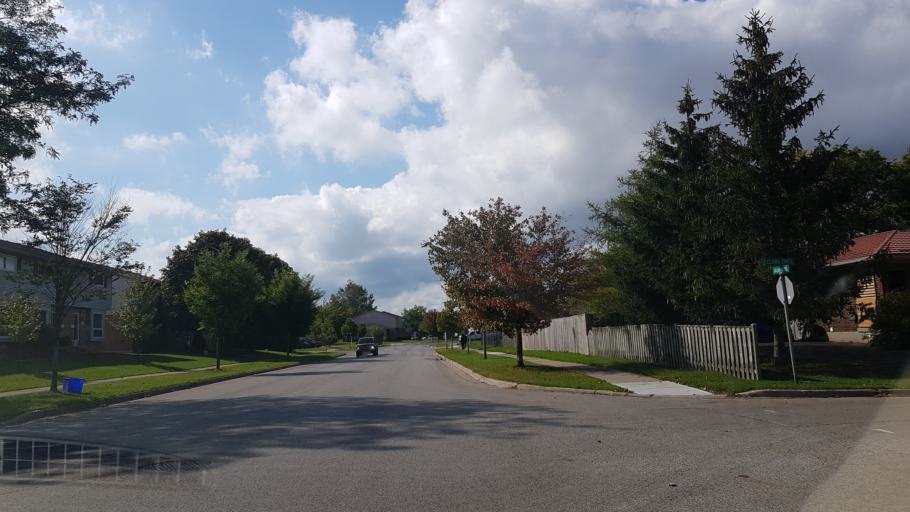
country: CA
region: Ontario
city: London
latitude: 42.9250
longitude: -81.2387
